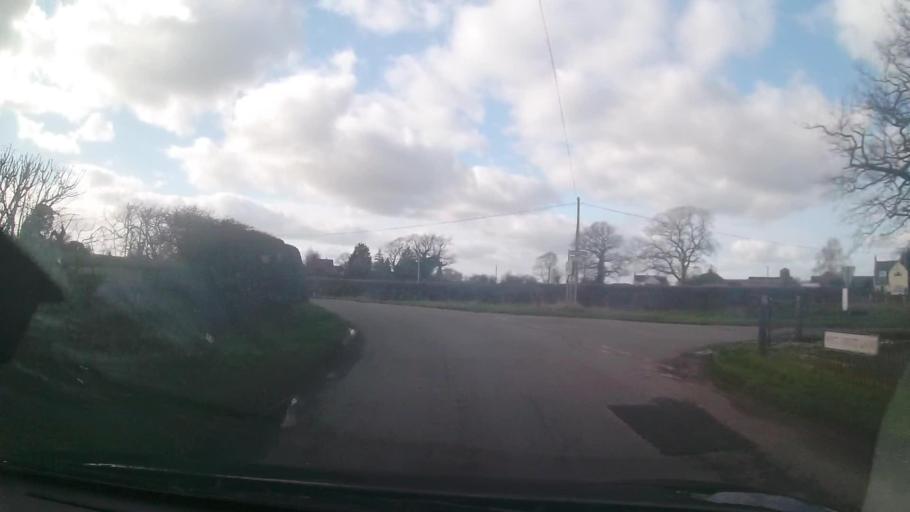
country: GB
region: England
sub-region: Shropshire
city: Wem
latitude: 52.9046
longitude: -2.7207
